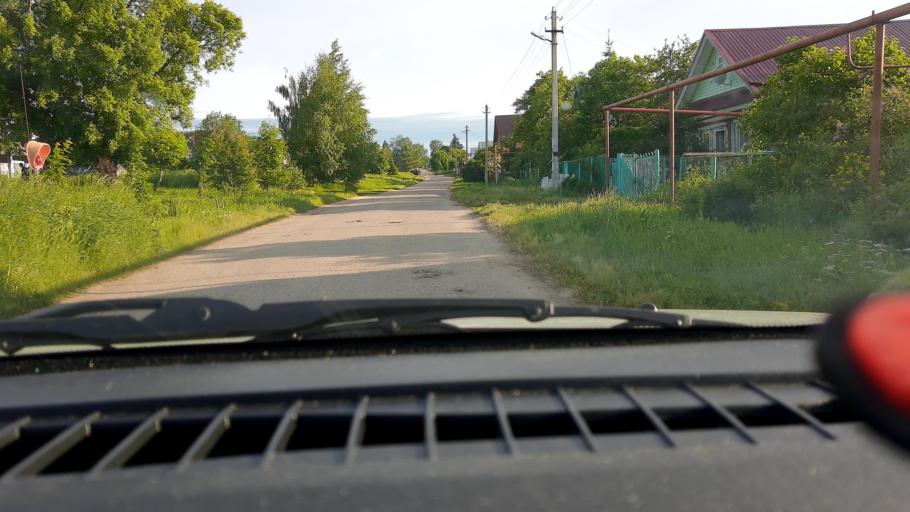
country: RU
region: Nizjnij Novgorod
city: Afonino
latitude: 56.1281
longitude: 44.0285
